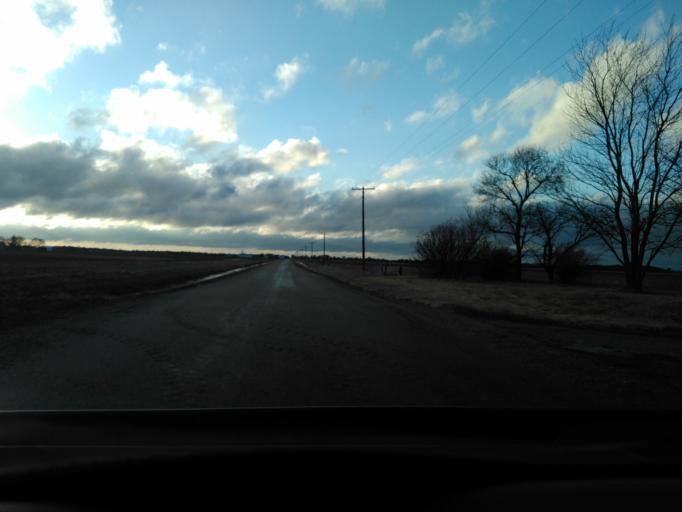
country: US
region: Illinois
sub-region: Effingham County
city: Altamont
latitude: 38.9579
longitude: -88.7228
